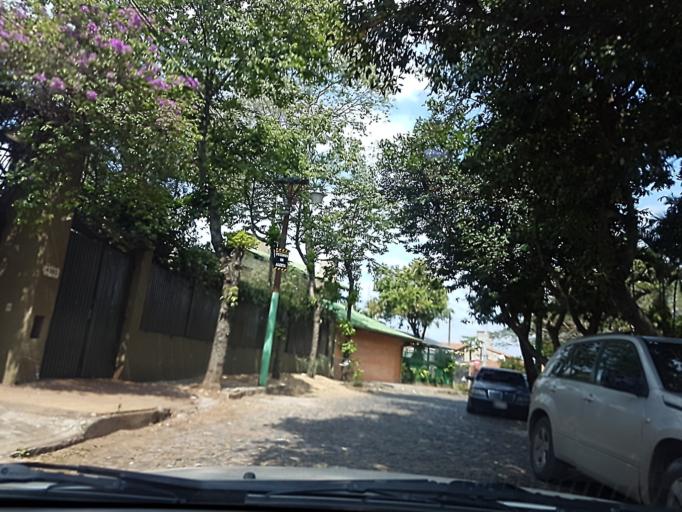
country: PY
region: Central
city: Lambare
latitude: -25.3310
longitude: -57.5781
